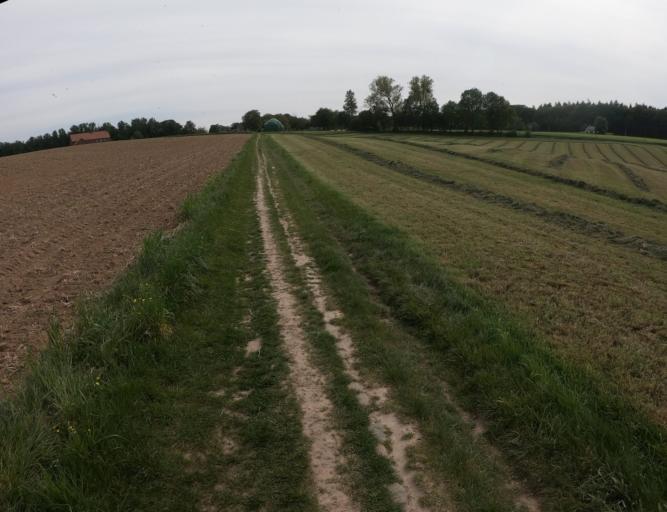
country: BE
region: Flanders
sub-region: Provincie Vlaams-Brabant
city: Beersel
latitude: 50.7457
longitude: 4.2989
